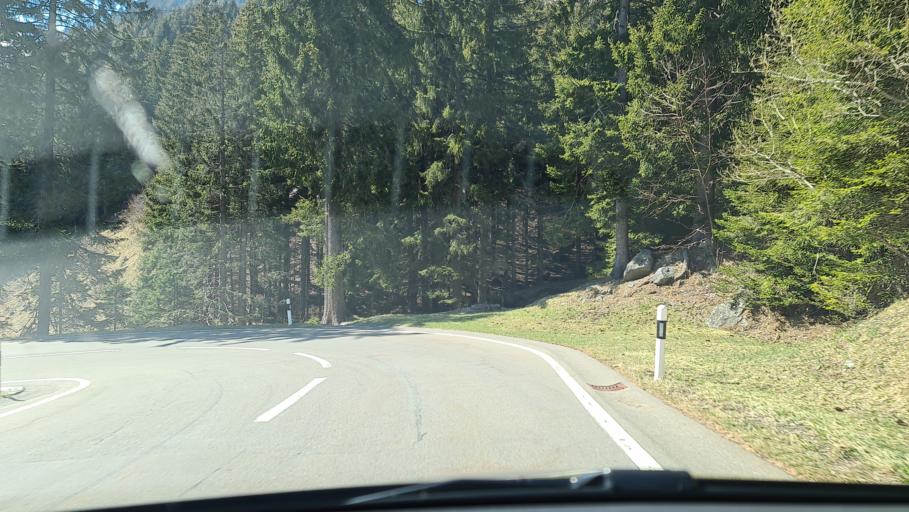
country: CH
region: Grisons
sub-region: Moesa District
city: Mesocco
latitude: 46.4324
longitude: 9.2149
